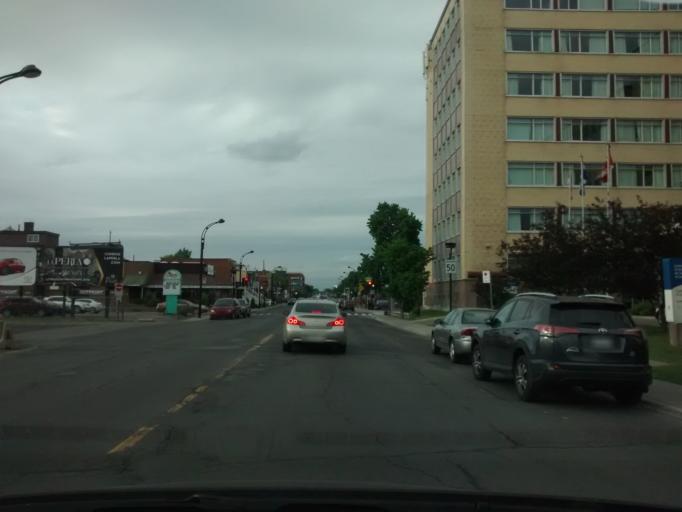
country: CA
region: Quebec
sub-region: Montreal
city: Saint-Leonard
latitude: 45.5620
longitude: -73.6111
